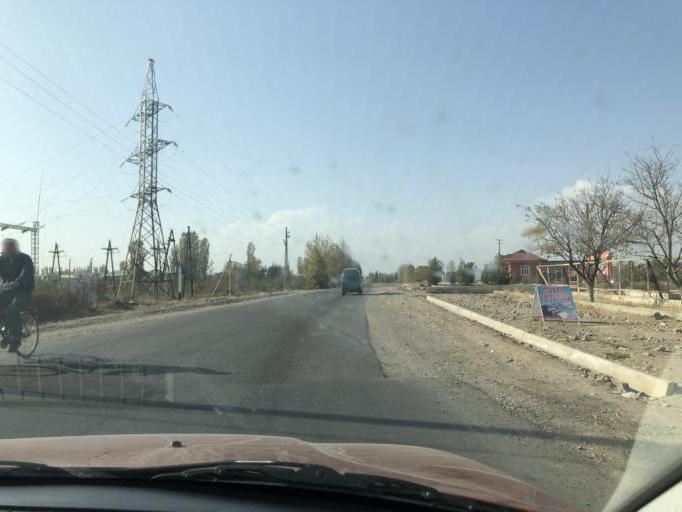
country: UZ
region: Namangan
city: Chust Shahri
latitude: 41.0744
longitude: 71.1999
